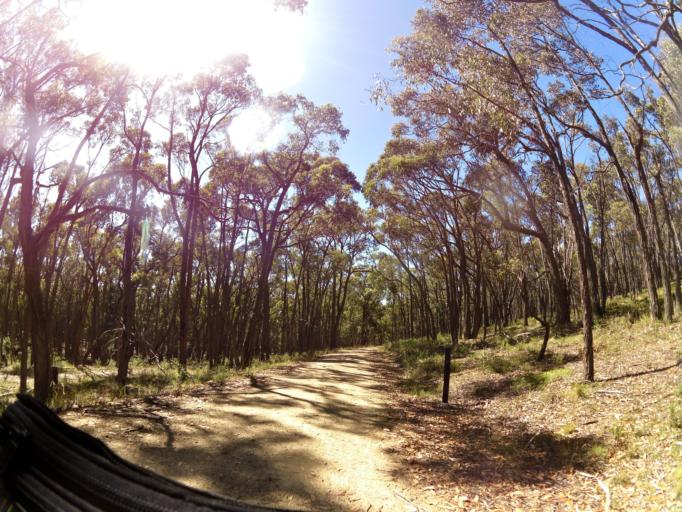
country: AU
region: Victoria
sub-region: Ballarat North
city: Delacombe
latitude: -37.6764
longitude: 143.5439
